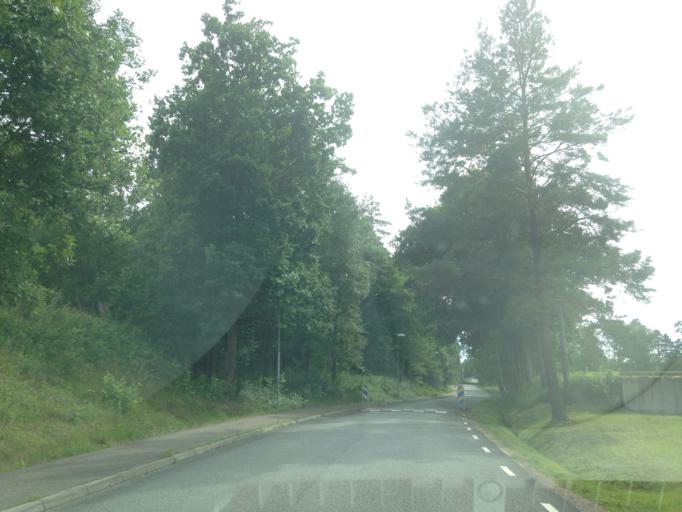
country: SE
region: Vaestra Goetaland
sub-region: Goteborg
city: Goeteborg
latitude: 57.7779
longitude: 11.9558
